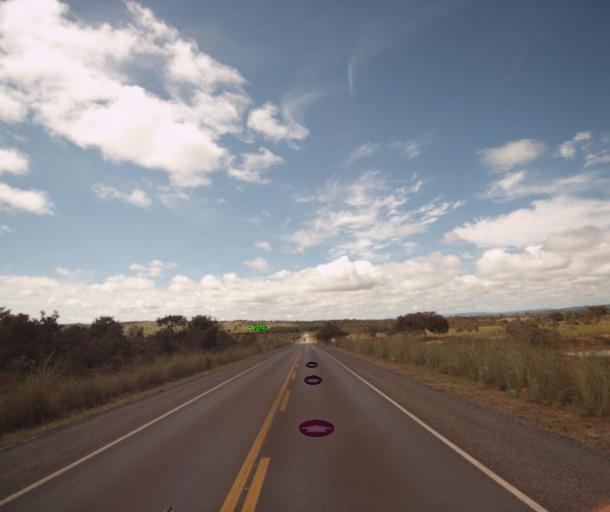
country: BR
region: Goias
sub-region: Padre Bernardo
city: Padre Bernardo
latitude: -15.2142
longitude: -48.5588
